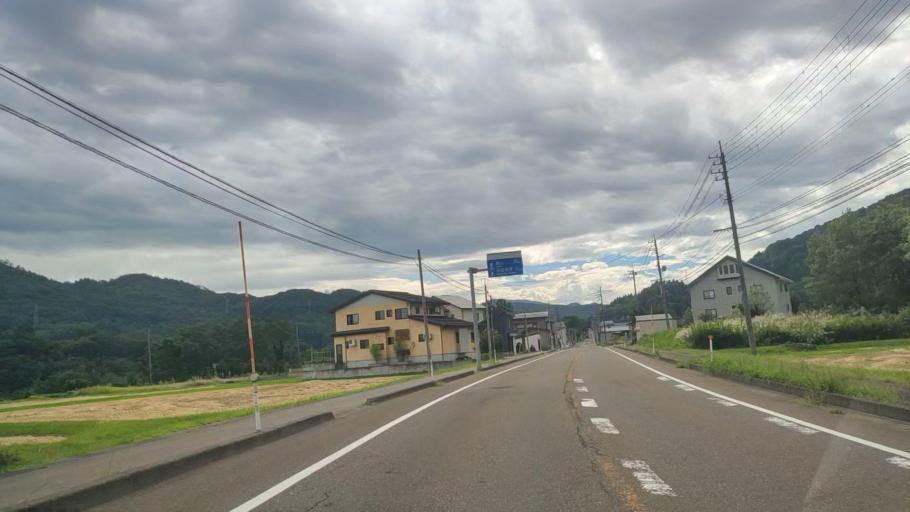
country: JP
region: Niigata
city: Arai
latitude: 37.0045
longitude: 138.2625
